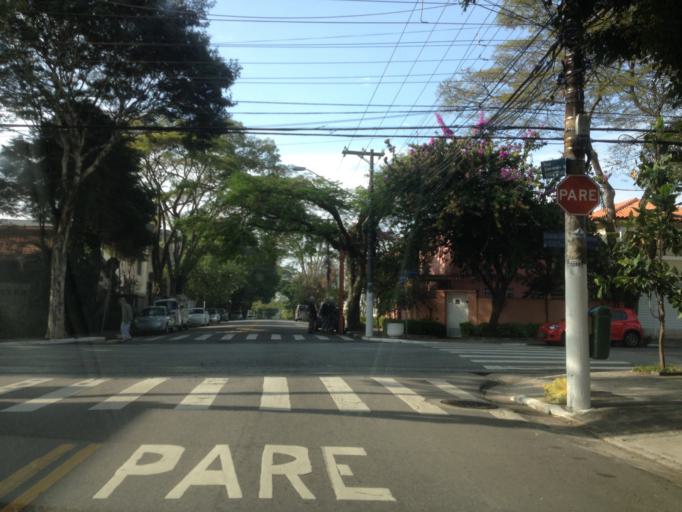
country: BR
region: Sao Paulo
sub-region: Sao Paulo
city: Sao Paulo
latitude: -23.6205
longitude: -46.6690
